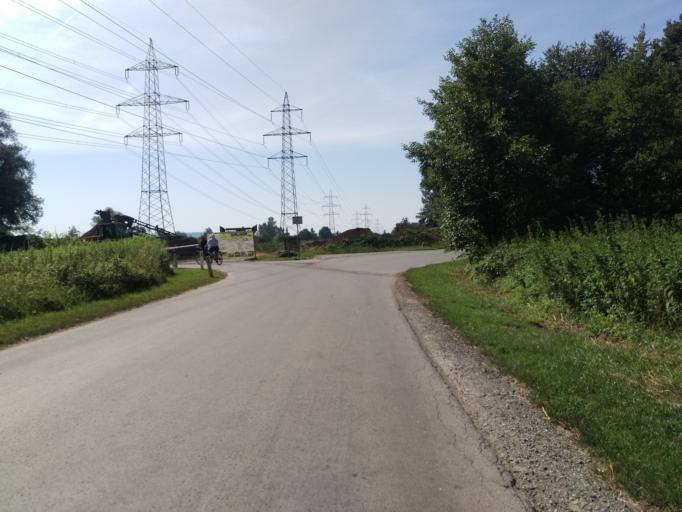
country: AT
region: Styria
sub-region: Politischer Bezirk Graz-Umgebung
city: Gossendorf
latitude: 46.9985
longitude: 15.4744
